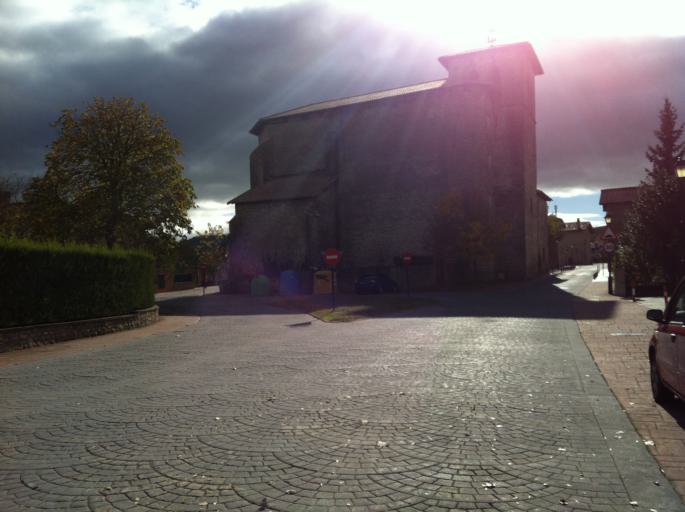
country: ES
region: Basque Country
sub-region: Provincia de Alava
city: Gasteiz / Vitoria
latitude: 42.8196
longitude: -2.6909
